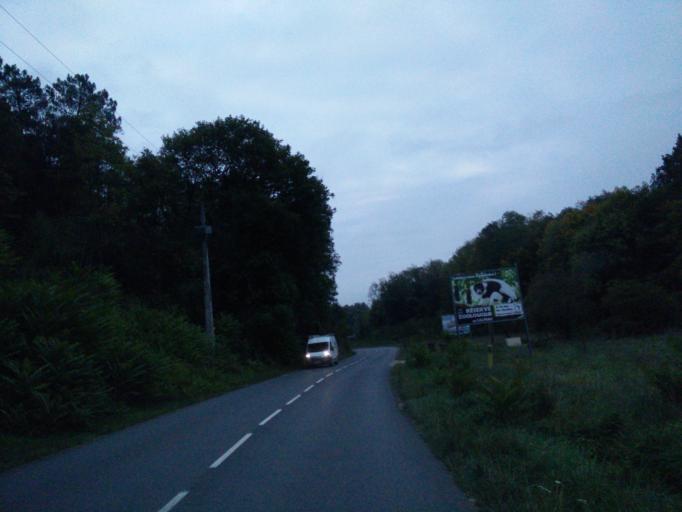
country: FR
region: Aquitaine
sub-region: Departement de la Dordogne
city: Sarlat-la-Caneda
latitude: 44.8715
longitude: 1.2410
